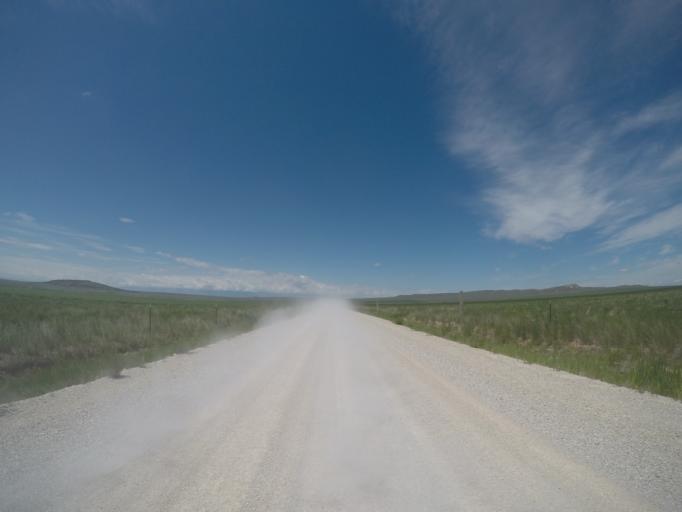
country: US
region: Montana
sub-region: Yellowstone County
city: Laurel
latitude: 45.2196
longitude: -108.7010
